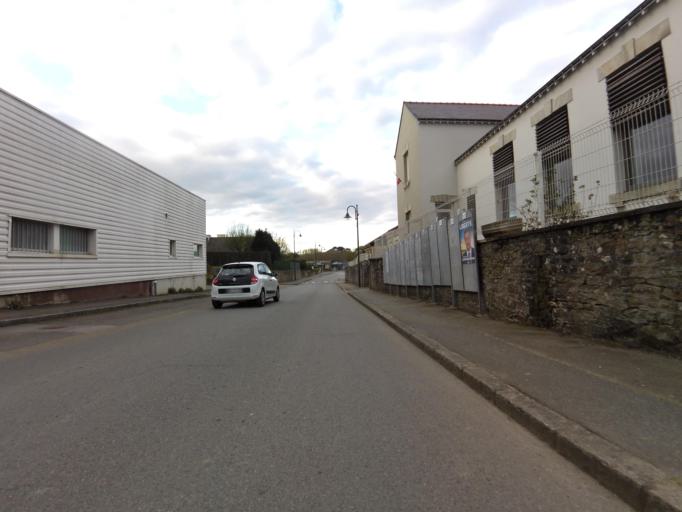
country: FR
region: Brittany
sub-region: Departement du Morbihan
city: Plougoumelen
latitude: 47.6536
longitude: -2.9169
